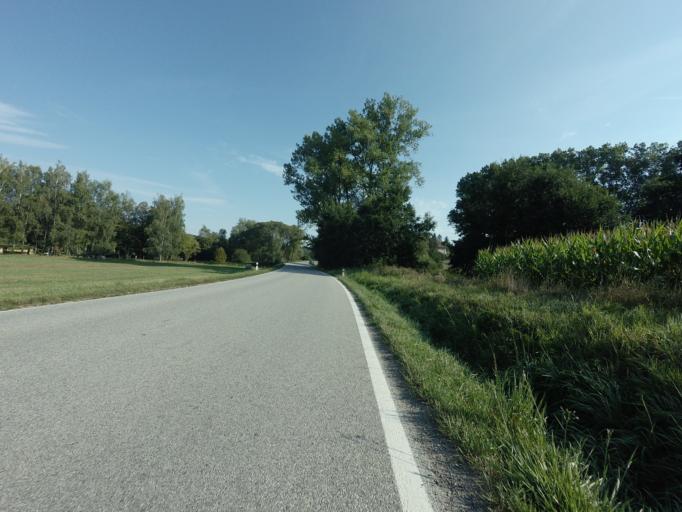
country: CZ
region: Jihocesky
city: Tyn nad Vltavou
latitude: 49.2463
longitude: 14.4199
